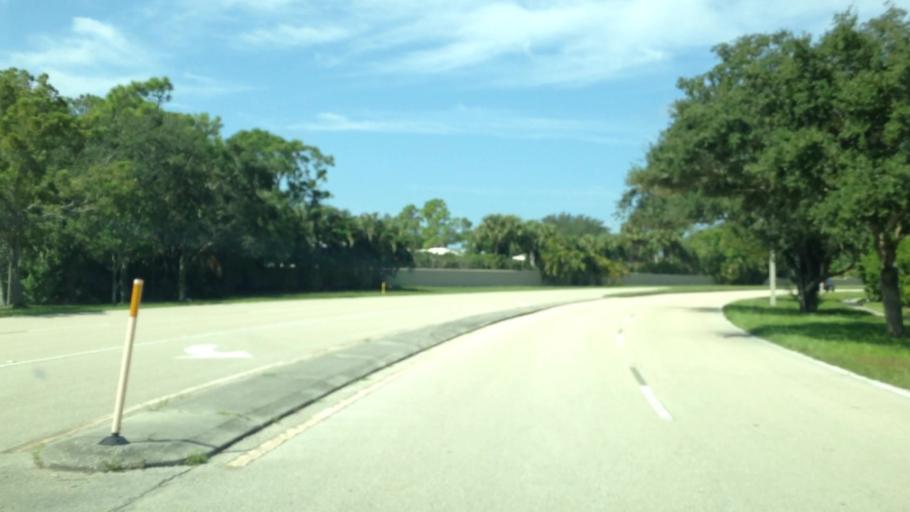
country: US
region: Florida
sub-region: Lee County
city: Bonita Springs
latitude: 26.3166
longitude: -81.8095
